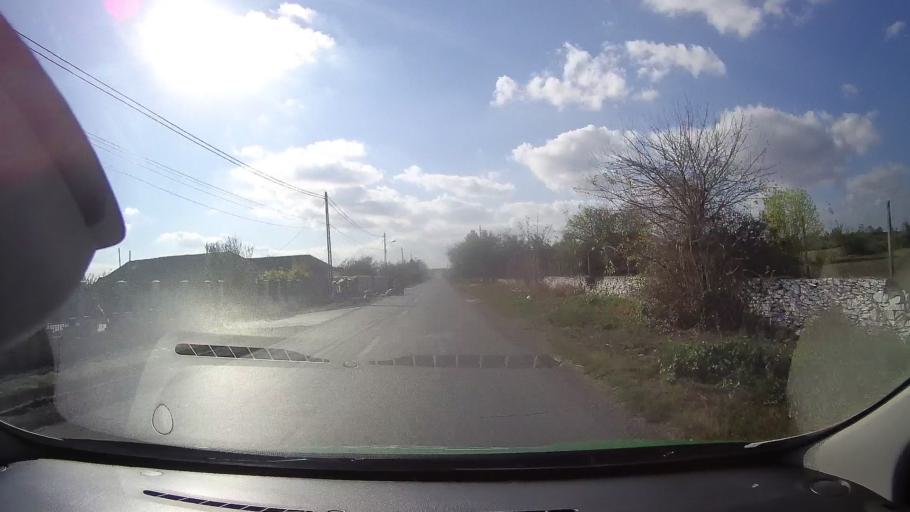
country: RO
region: Constanta
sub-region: Comuna Mihai Viteazu
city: Mihai Viteazu
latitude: 44.6247
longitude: 28.7310
